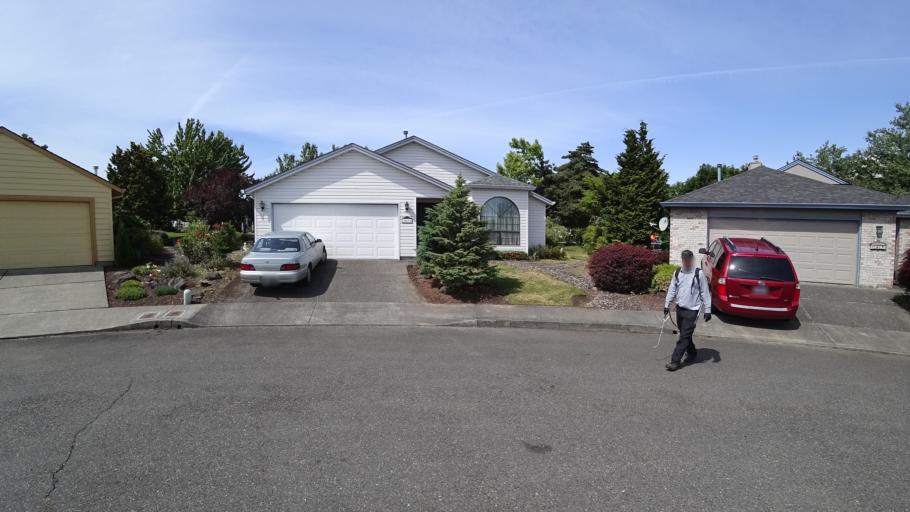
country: US
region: Oregon
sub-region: Multnomah County
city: Fairview
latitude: 45.5409
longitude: -122.5018
